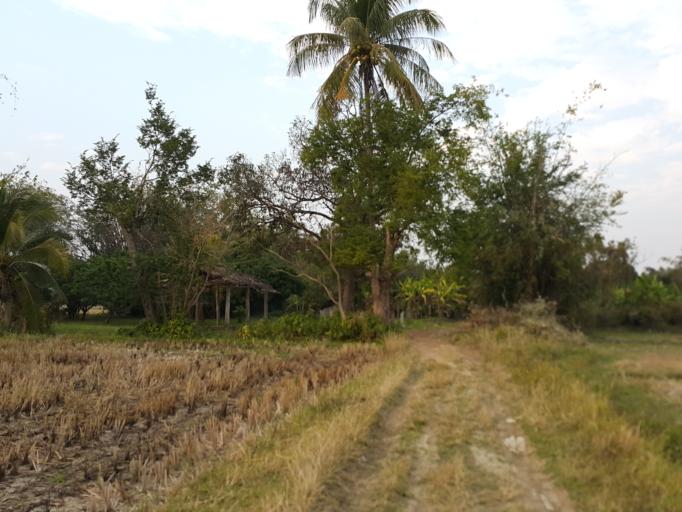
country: TH
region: Chiang Mai
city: San Sai
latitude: 18.8903
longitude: 99.1358
